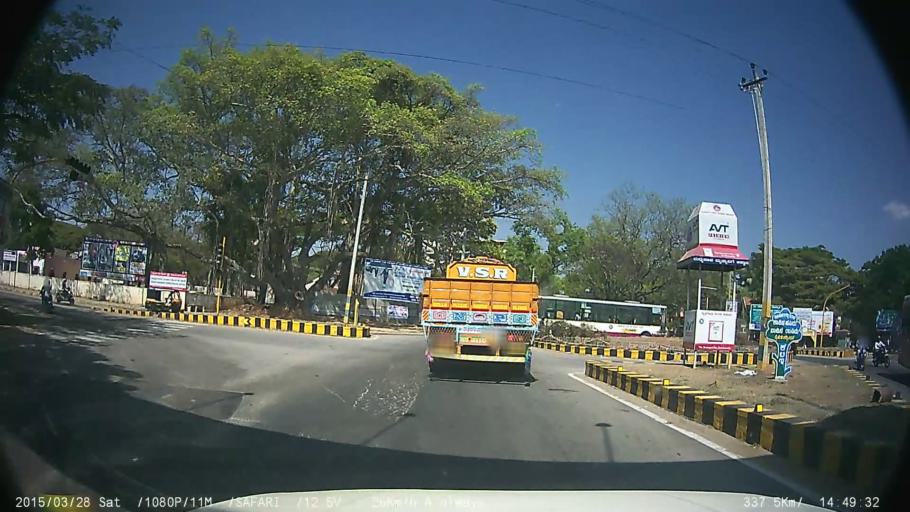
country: IN
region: Karnataka
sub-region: Mysore
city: Mysore
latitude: 12.2992
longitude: 76.6787
